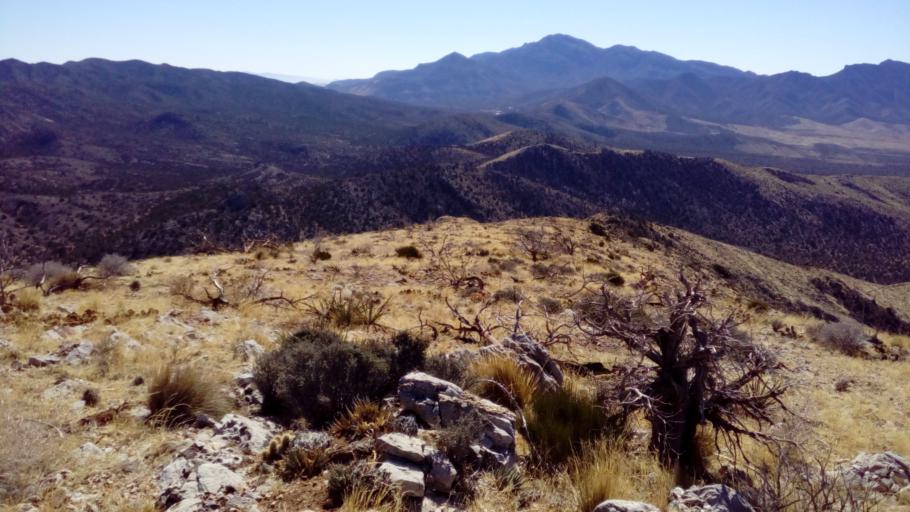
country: US
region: Nevada
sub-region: Clark County
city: Summerlin South
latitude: 36.0704
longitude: -115.5188
